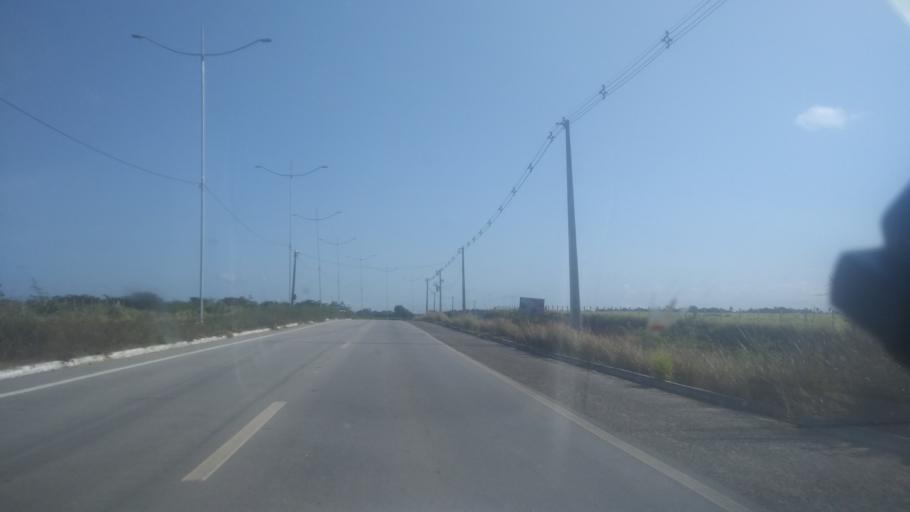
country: BR
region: Rio Grande do Norte
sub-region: Macaiba
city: Macaiba
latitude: -5.8631
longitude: -35.3786
